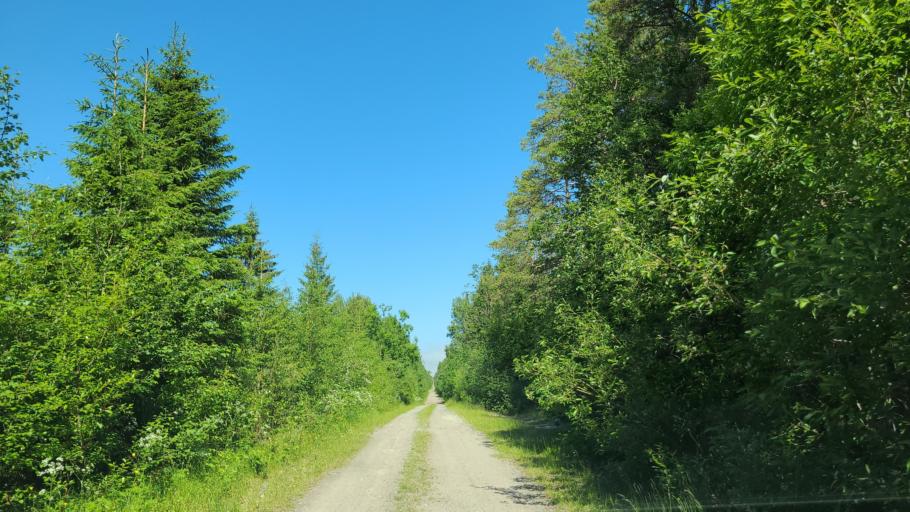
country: SE
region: Vaesternorrland
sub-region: OErnskoeldsviks Kommun
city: Husum
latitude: 63.4206
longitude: 19.2232
